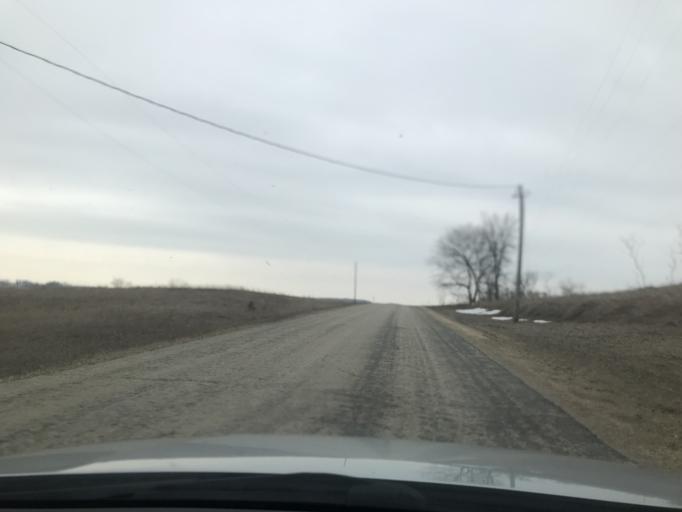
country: US
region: Wisconsin
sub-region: Marinette County
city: Peshtigo
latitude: 45.0967
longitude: -87.9324
